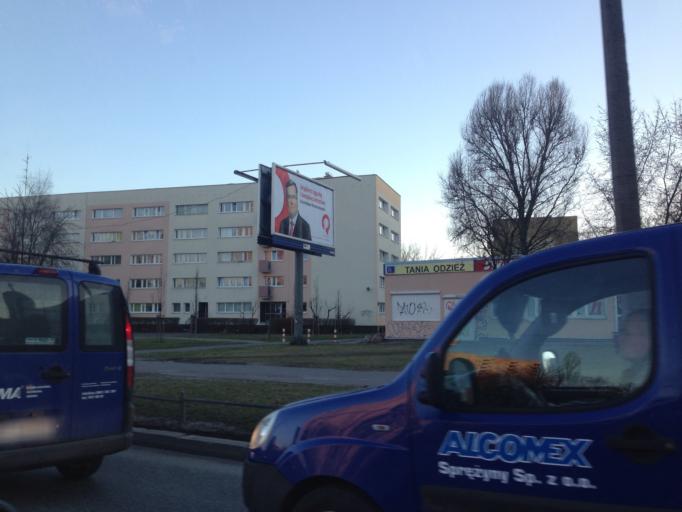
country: PL
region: Masovian Voivodeship
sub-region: Warszawa
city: Mokotow
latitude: 52.1703
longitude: 21.0081
